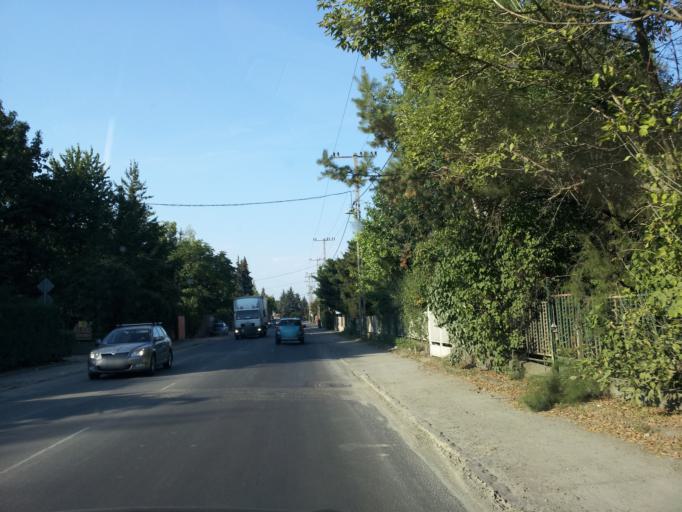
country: HU
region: Pest
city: Szentendre
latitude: 47.6843
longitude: 19.0821
